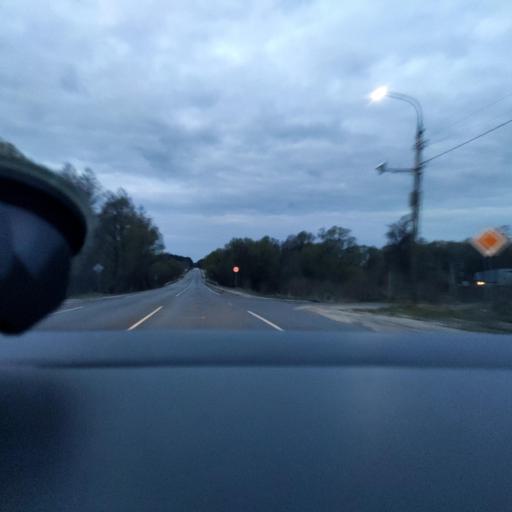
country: RU
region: Moskovskaya
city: Krasnyy Tkach
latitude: 55.4257
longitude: 39.1919
